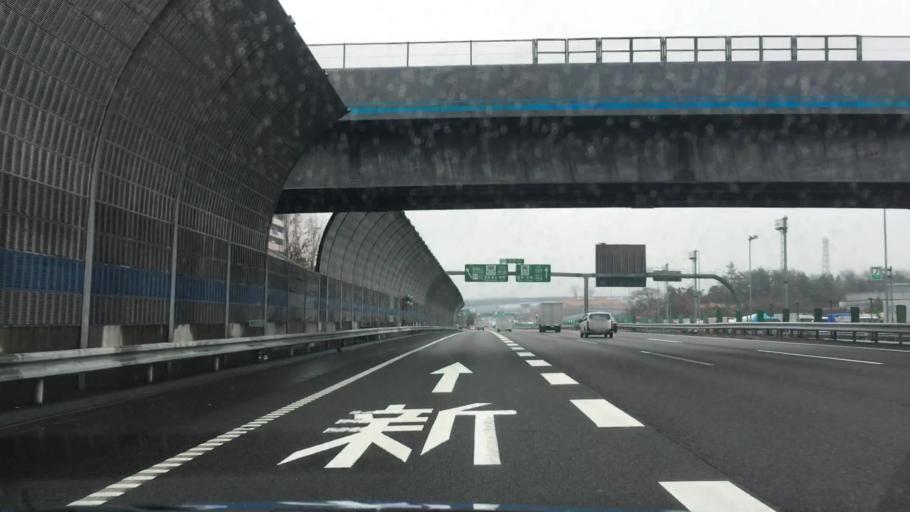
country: JP
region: Shiga Prefecture
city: Kusatsu
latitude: 34.9785
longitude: 135.9494
